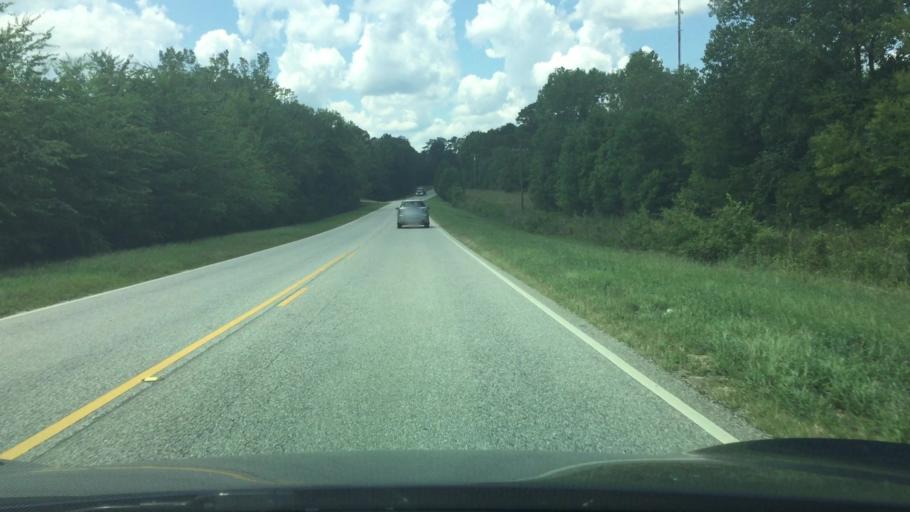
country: US
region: Alabama
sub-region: Montgomery County
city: Pike Road
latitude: 32.1968
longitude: -86.1096
